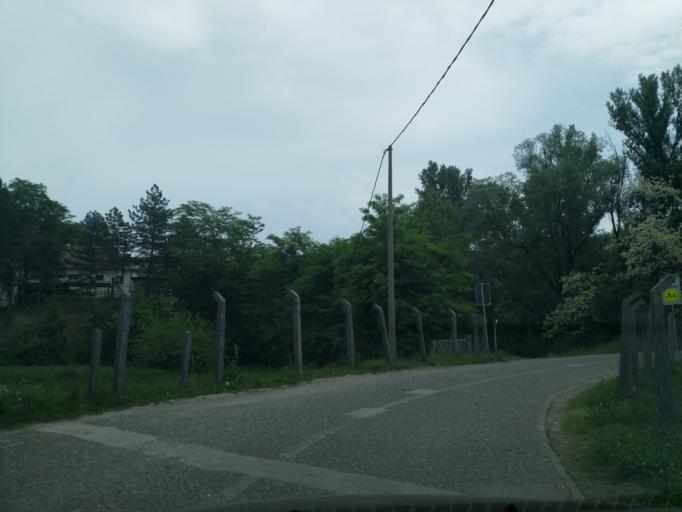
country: RS
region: Central Serbia
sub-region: Pomoravski Okrug
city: Paracin
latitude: 43.8563
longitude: 21.5978
